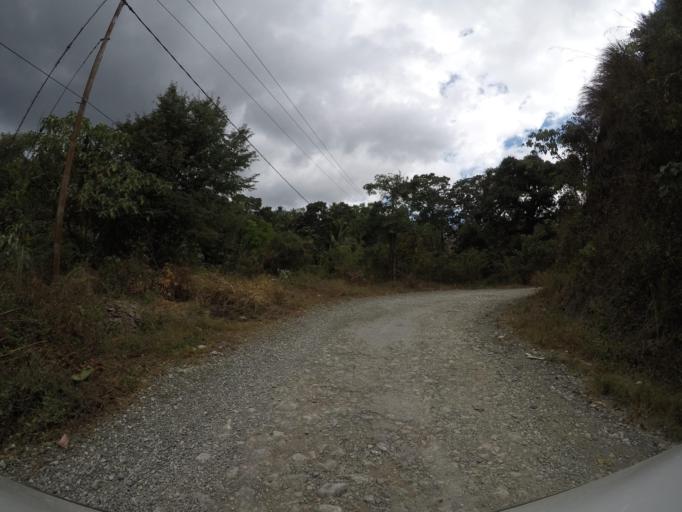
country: TL
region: Baucau
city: Baucau
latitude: -8.6225
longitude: 126.6573
